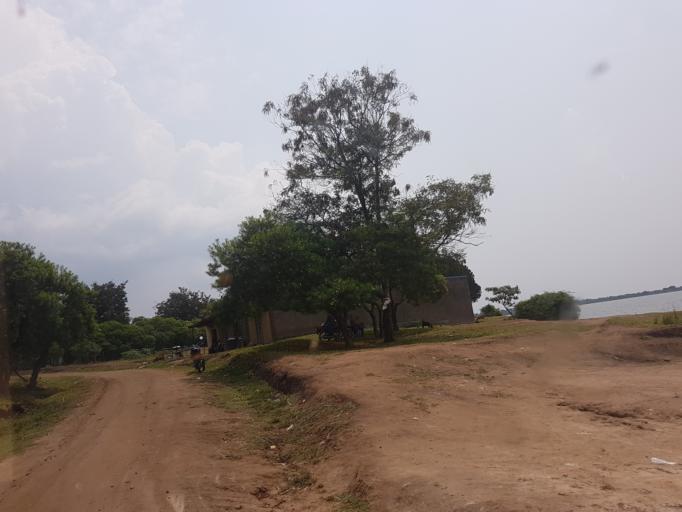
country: UG
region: Western Region
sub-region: Rubirizi District
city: Rubirizi
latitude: -0.0741
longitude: 30.1802
